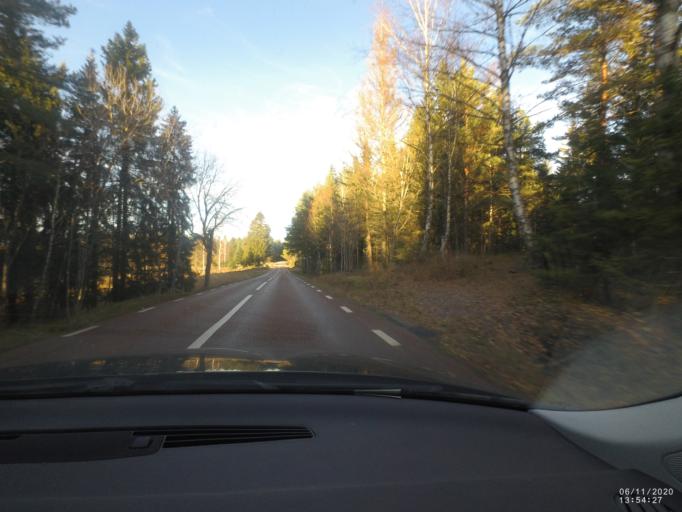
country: SE
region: Soedermanland
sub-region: Gnesta Kommun
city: Gnesta
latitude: 58.9706
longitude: 17.1465
